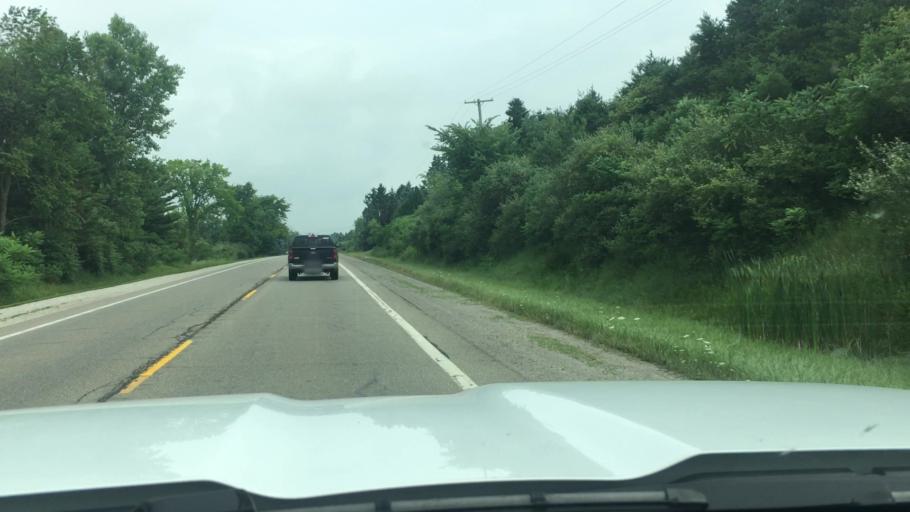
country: US
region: Michigan
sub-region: Sanilac County
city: Brown City
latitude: 43.1698
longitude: -83.0758
